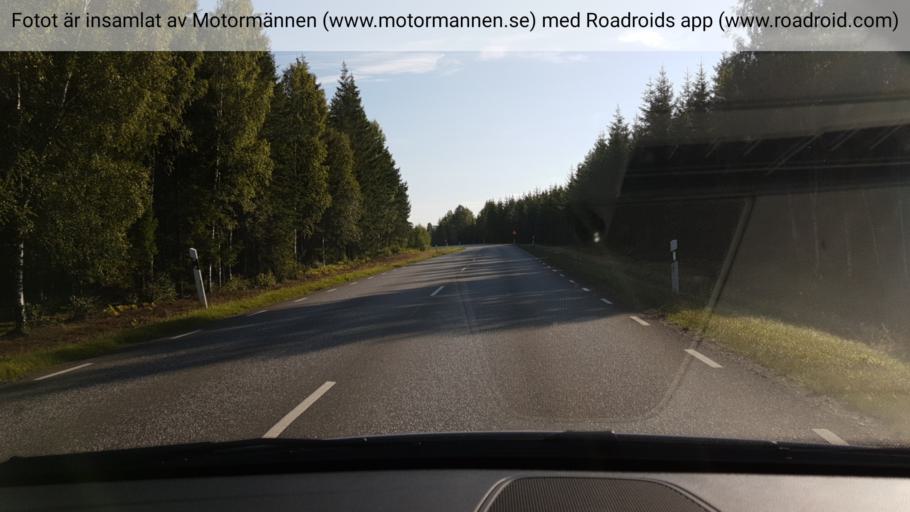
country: SE
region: Vaestra Goetaland
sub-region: Tidaholms Kommun
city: Tidaholm
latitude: 58.1935
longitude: 13.9141
